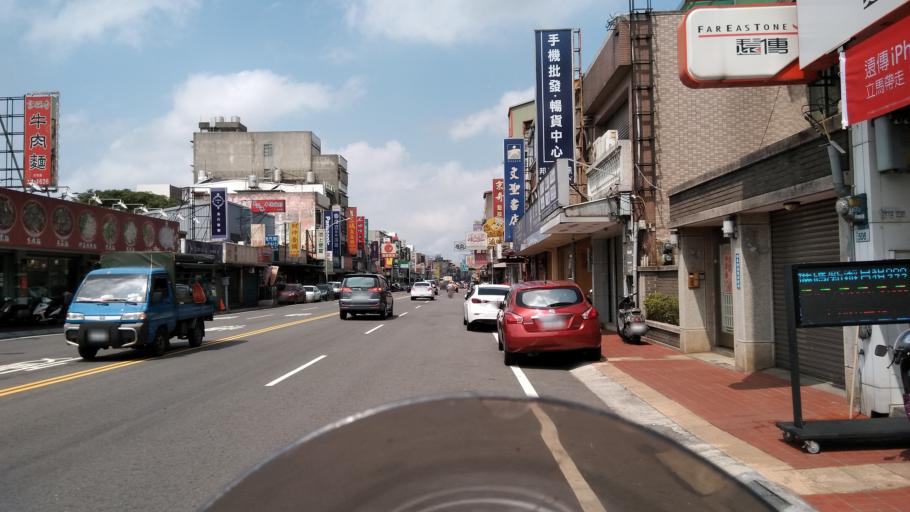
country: TW
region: Taiwan
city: Taoyuan City
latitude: 25.0233
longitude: 121.2605
